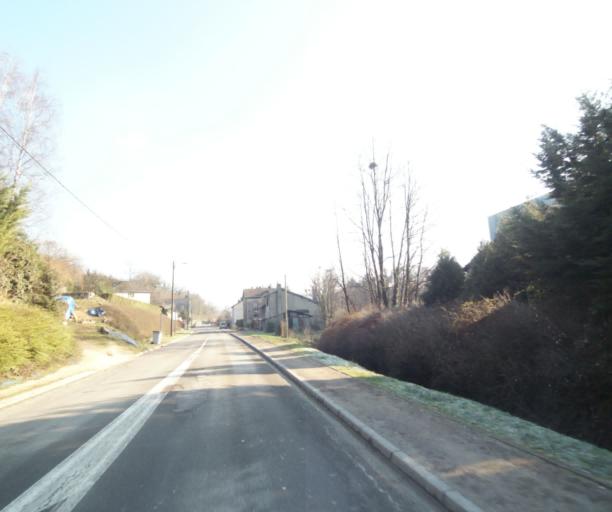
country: FR
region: Champagne-Ardenne
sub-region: Departement de la Haute-Marne
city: Wassy
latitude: 48.4938
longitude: 4.9576
